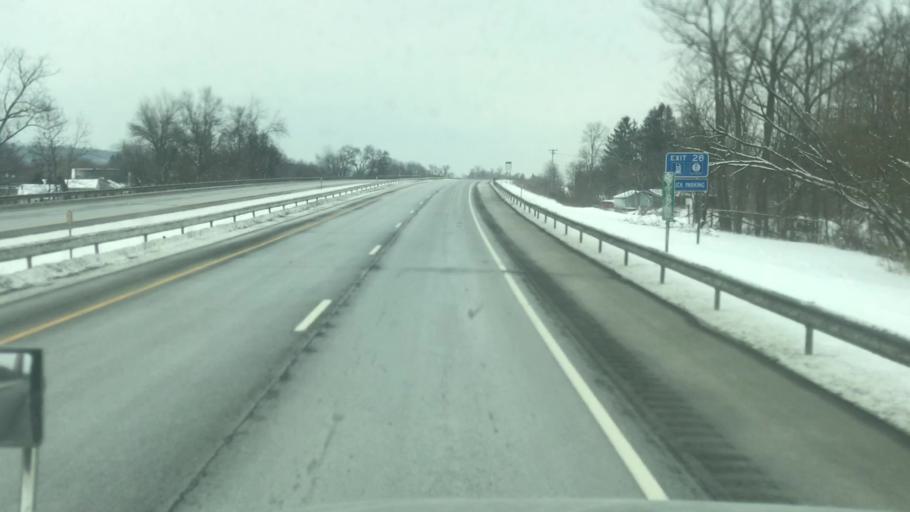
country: US
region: New York
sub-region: Montgomery County
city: Fonda
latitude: 42.9480
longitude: -74.3760
